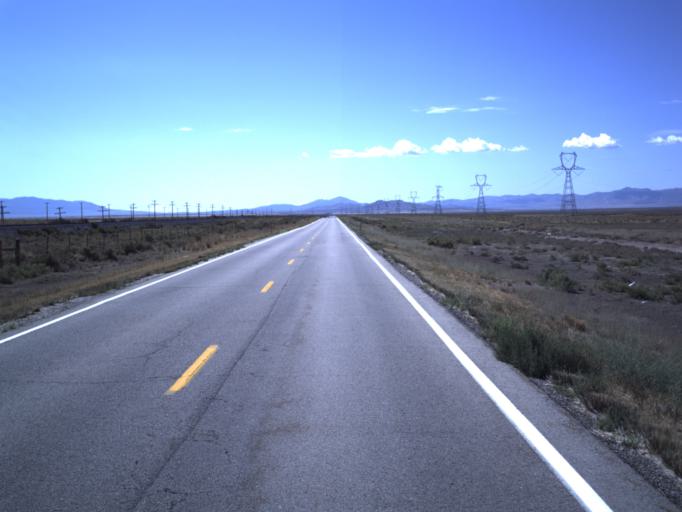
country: US
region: Utah
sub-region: Tooele County
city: Tooele
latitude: 40.3086
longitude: -112.4041
